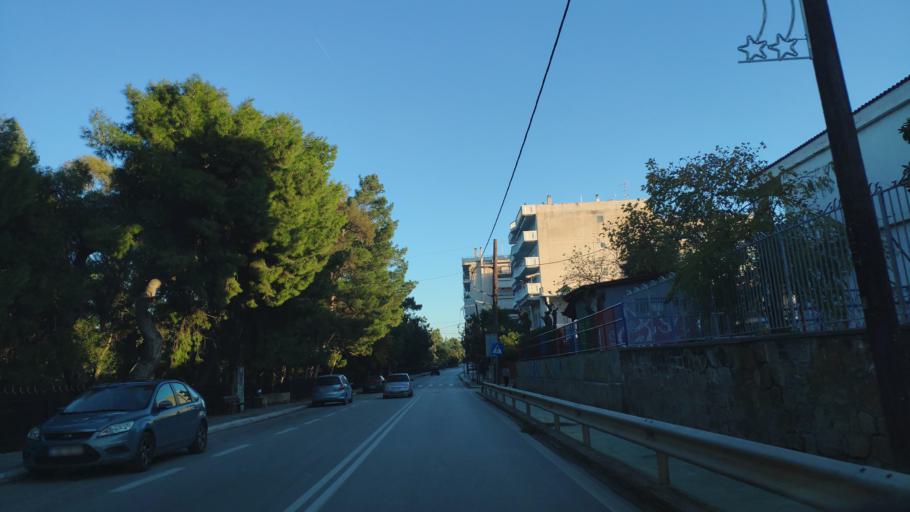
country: GR
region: Peloponnese
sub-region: Nomos Korinthias
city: Xylokastro
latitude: 38.0754
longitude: 22.6390
